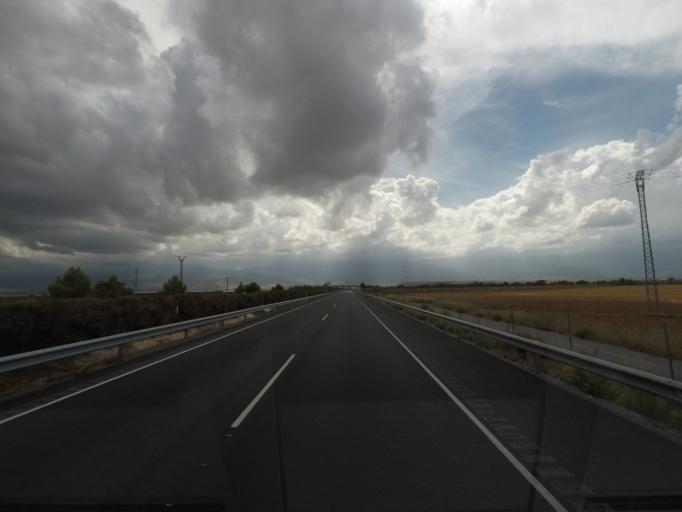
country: ES
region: Andalusia
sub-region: Provincia de Granada
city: Albunan
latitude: 37.2512
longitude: -3.0817
